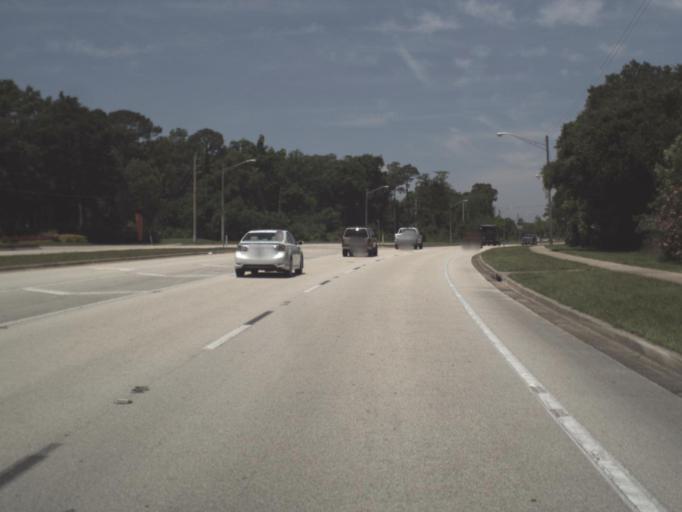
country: US
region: Florida
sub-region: Saint Johns County
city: Fruit Cove
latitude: 30.2158
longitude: -81.5445
